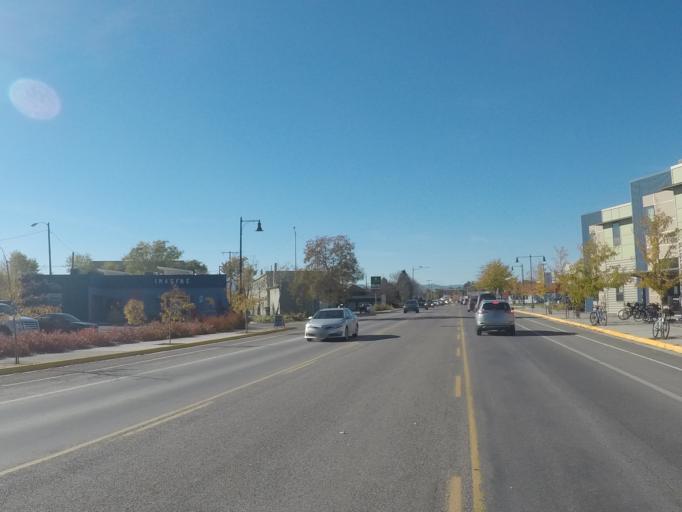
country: US
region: Montana
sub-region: Missoula County
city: Missoula
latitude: 46.8765
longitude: -114.0087
